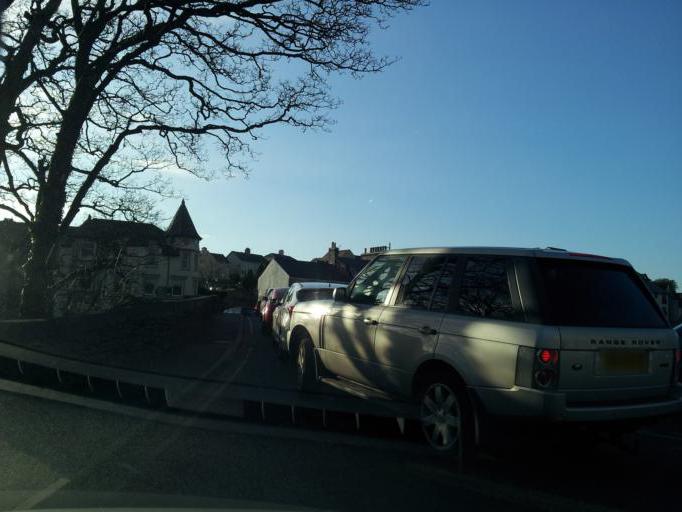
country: GB
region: England
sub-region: Cumbria
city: Kendal
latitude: 54.3206
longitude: -2.7440
